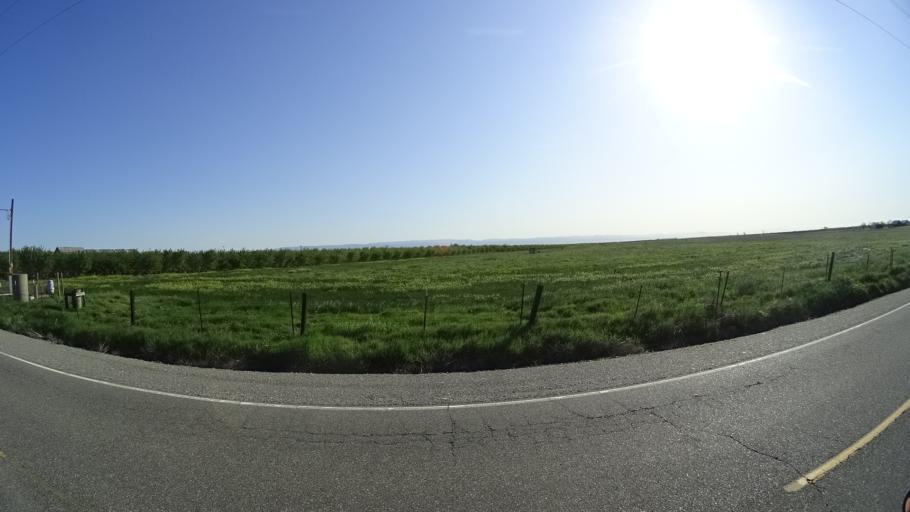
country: US
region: California
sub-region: Glenn County
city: Orland
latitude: 39.7603
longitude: -122.1055
